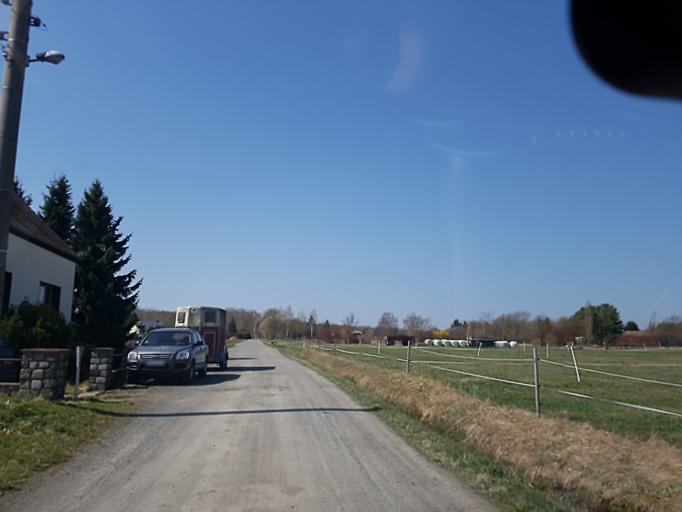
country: DE
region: Brandenburg
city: Schonborn
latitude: 51.5943
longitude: 13.4986
